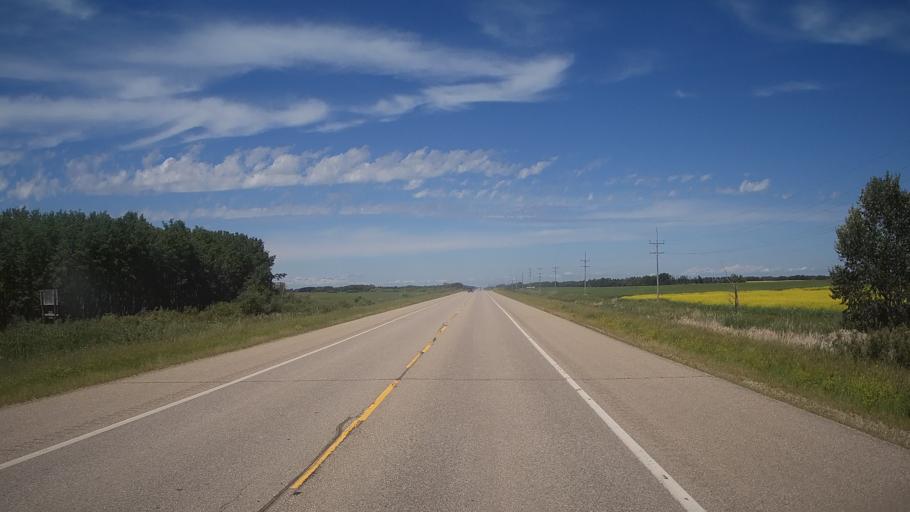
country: CA
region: Saskatchewan
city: Langenburg
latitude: 50.6444
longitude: -101.2759
